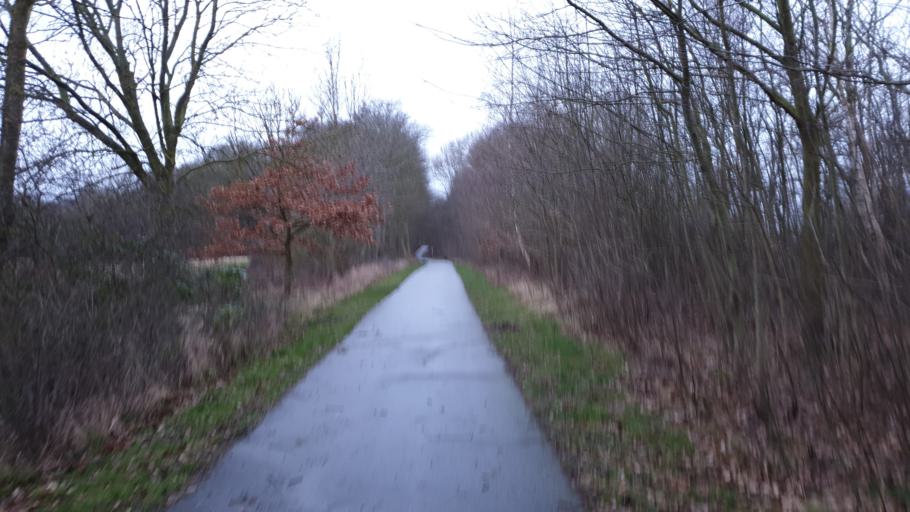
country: DE
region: Mecklenburg-Vorpommern
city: Kalkhorst
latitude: 53.9985
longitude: 11.0173
